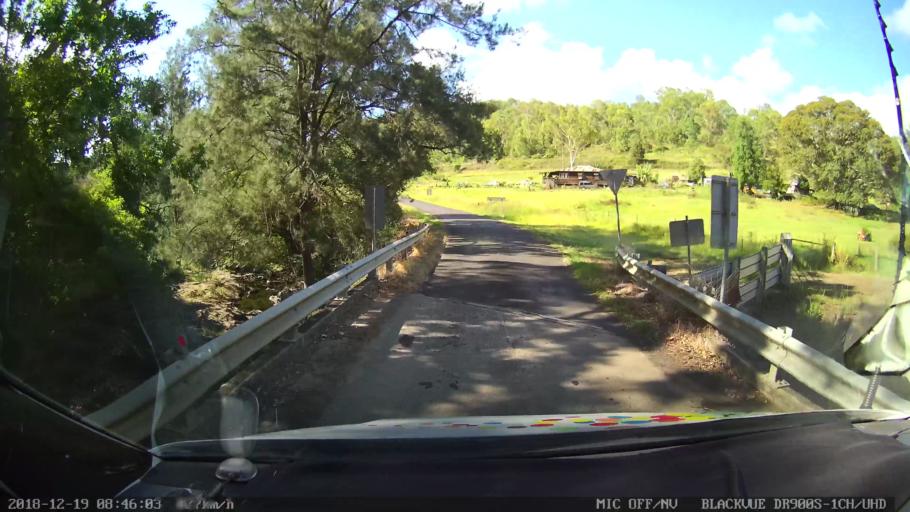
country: AU
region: New South Wales
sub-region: Kyogle
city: Kyogle
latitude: -28.3595
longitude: 152.9675
